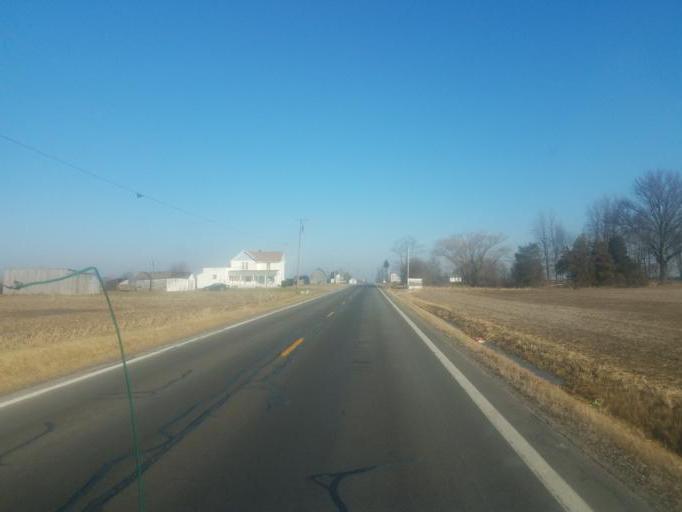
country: US
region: Ohio
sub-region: Crawford County
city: Bucyrus
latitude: 40.9677
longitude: -82.9355
